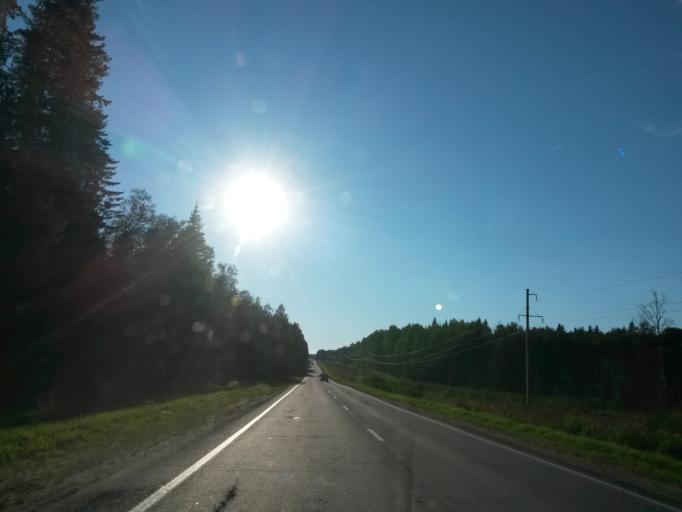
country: RU
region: Jaroslavl
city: Gavrilov-Yam
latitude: 57.2667
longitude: 39.9939
